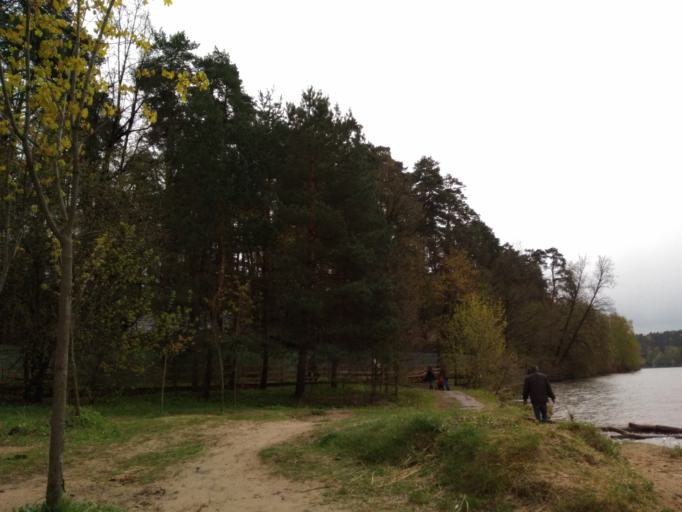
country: RU
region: Moscow
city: Strogino
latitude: 55.7854
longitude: 37.4078
